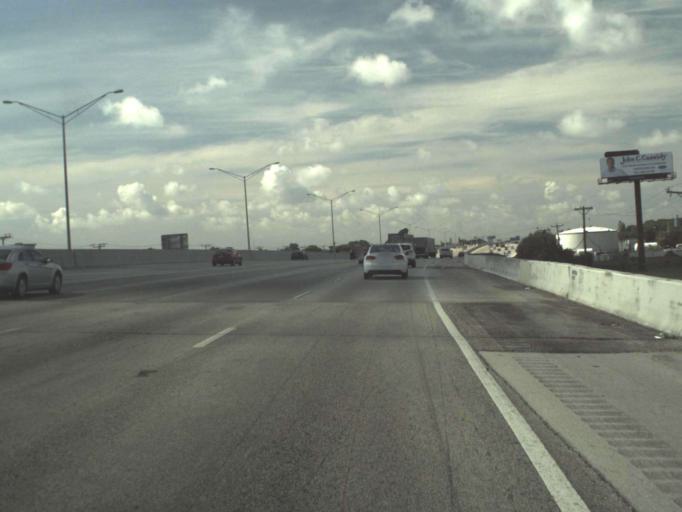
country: US
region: Florida
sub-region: Palm Beach County
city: North Palm Beach
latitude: 26.8311
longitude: -80.0978
